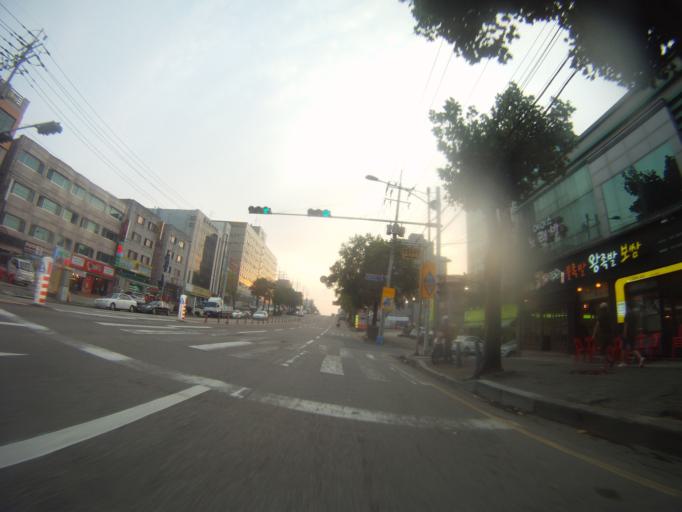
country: KR
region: Incheon
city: Incheon
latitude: 37.4581
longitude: 126.6849
